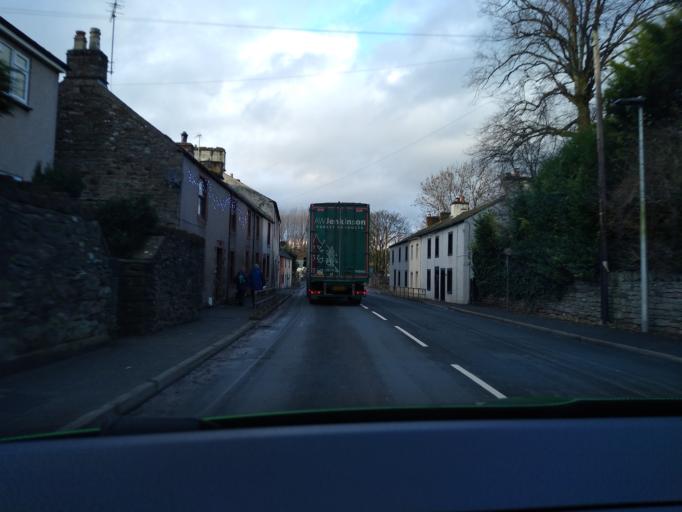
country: GB
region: England
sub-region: Cumbria
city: Penrith
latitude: 54.6504
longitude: -2.7411
